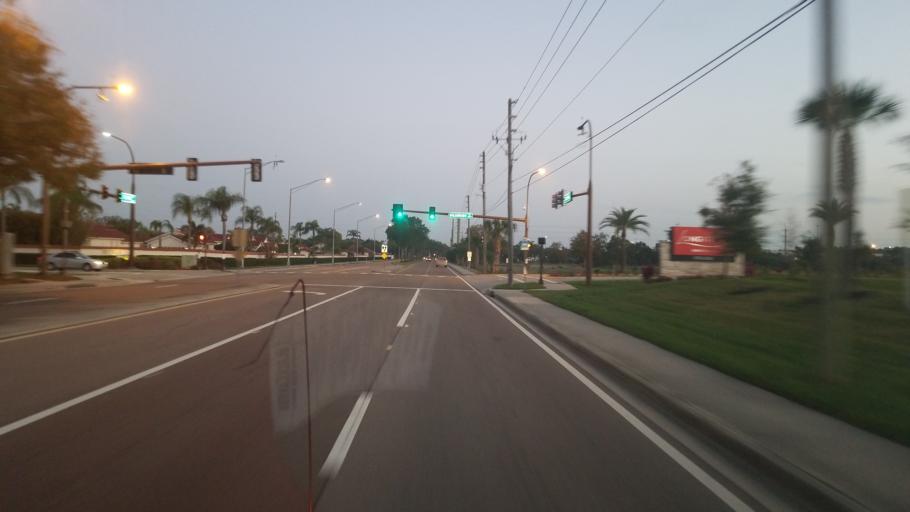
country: US
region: Florida
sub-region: Sarasota County
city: Lake Sarasota
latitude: 27.2884
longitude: -82.4521
